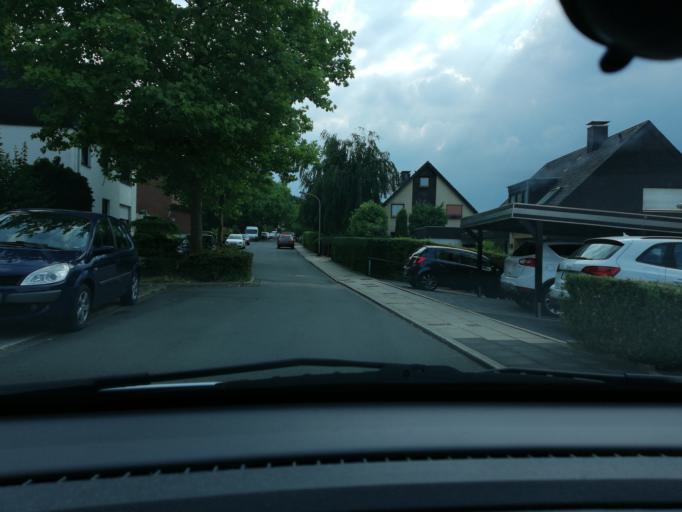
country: DE
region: North Rhine-Westphalia
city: Wetter (Ruhr)
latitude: 51.3771
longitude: 7.3691
